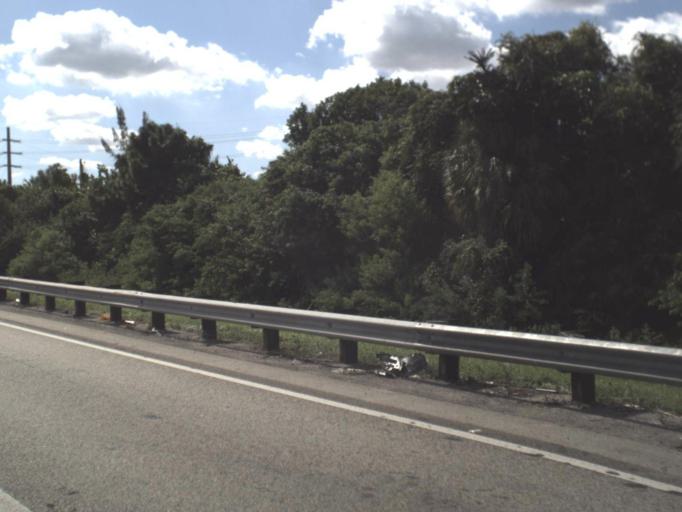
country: US
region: Florida
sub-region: Broward County
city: Pembroke Pines
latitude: 26.0055
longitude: -80.2151
